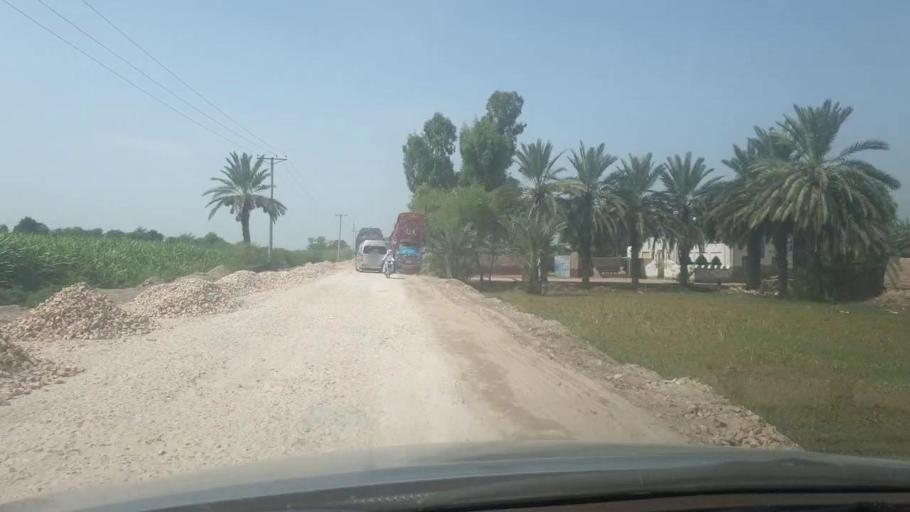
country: PK
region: Sindh
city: Ranipur
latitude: 27.2779
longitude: 68.5990
